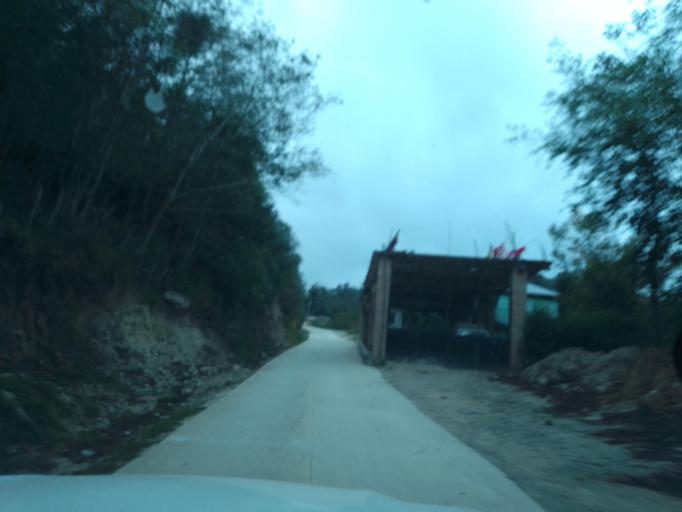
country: MX
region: Chiapas
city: Motozintla de Mendoza
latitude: 15.2242
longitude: -92.2385
